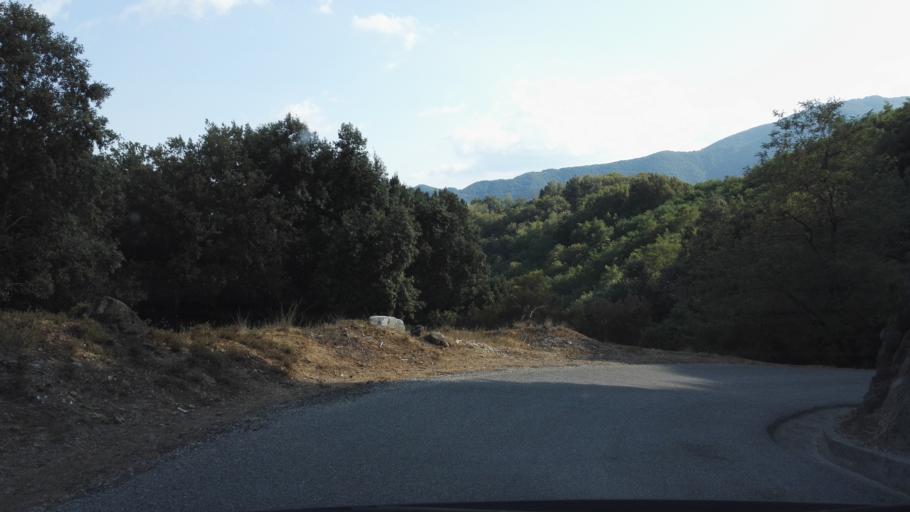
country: IT
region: Calabria
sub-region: Provincia di Vibo-Valentia
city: Nardodipace
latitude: 38.4550
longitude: 16.3471
